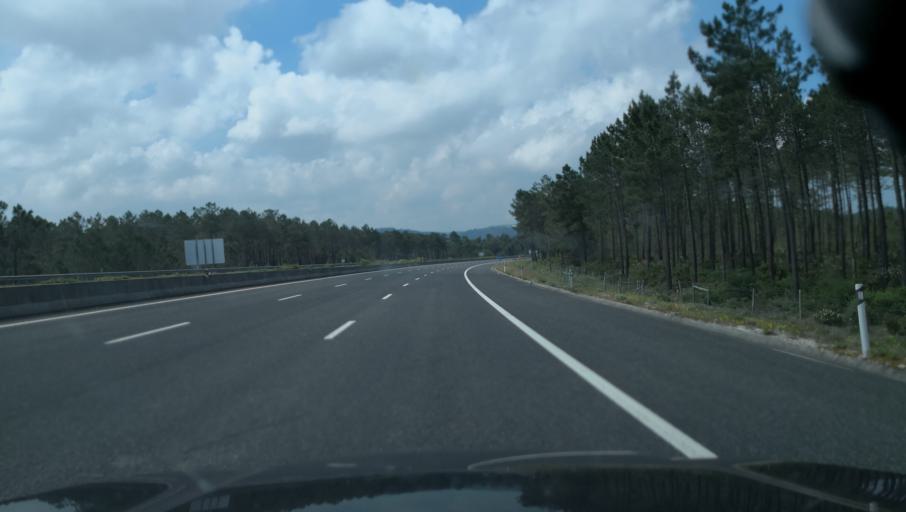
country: PT
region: Leiria
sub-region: Alcobaca
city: Alcobaca
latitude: 39.5957
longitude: -9.0016
